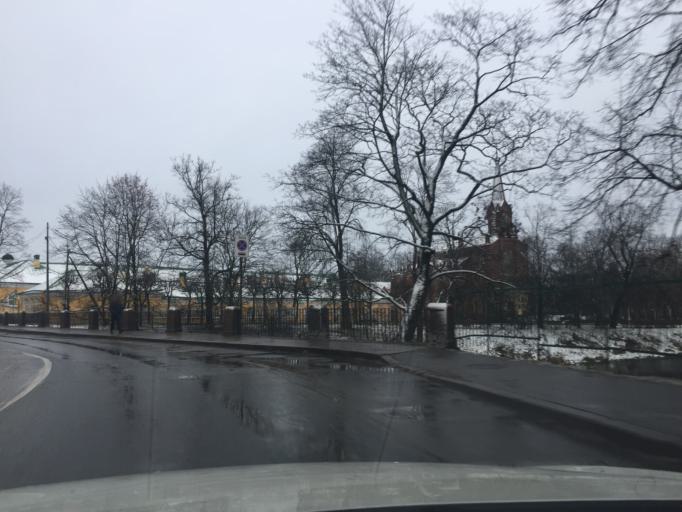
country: RU
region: St.-Petersburg
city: Pushkin
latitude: 59.7132
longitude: 30.4096
